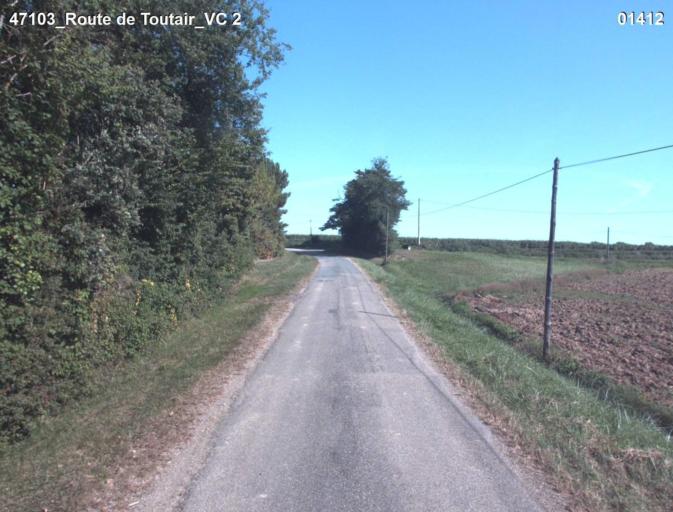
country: FR
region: Aquitaine
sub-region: Departement du Lot-et-Garonne
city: Nerac
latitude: 44.0755
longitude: 0.3297
